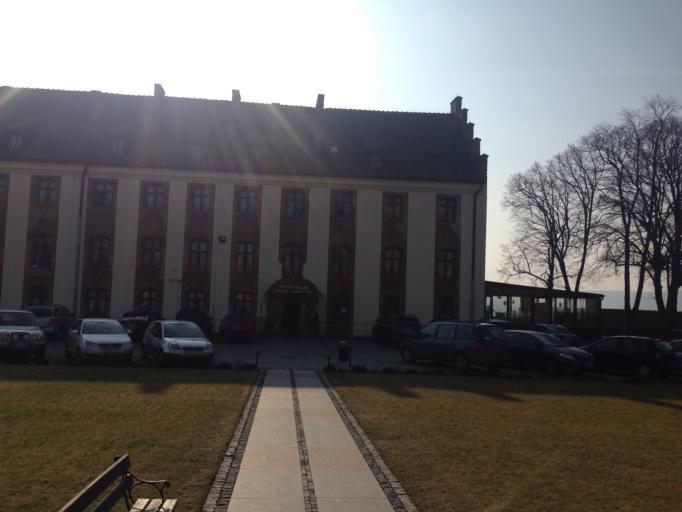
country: PL
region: Pomeranian Voivodeship
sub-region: Powiat tczewski
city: Gniew
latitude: 53.8339
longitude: 18.8290
